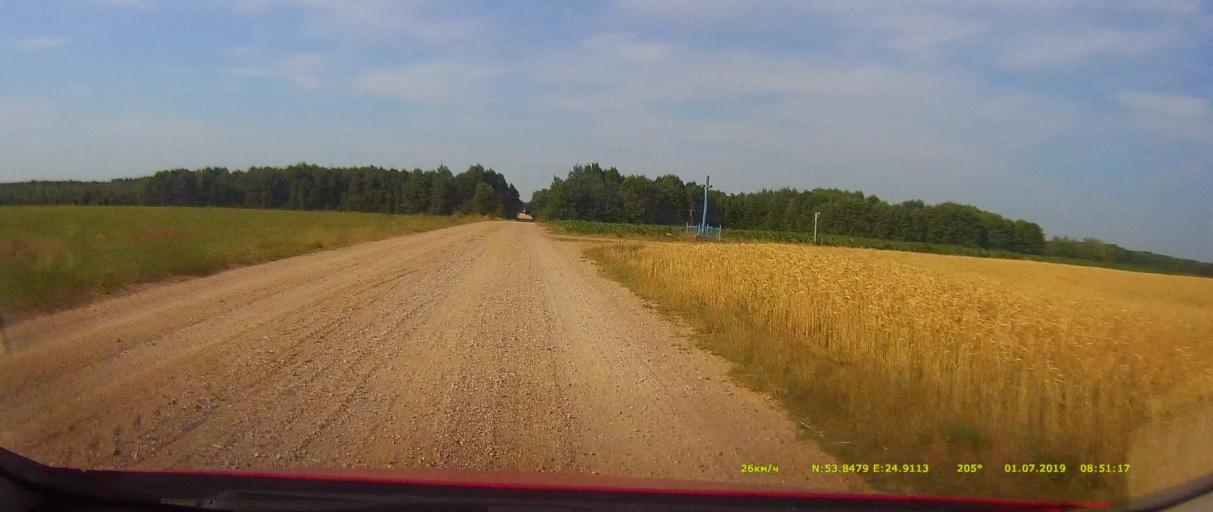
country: BY
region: Grodnenskaya
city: Shchuchin
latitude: 53.8480
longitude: 24.9113
